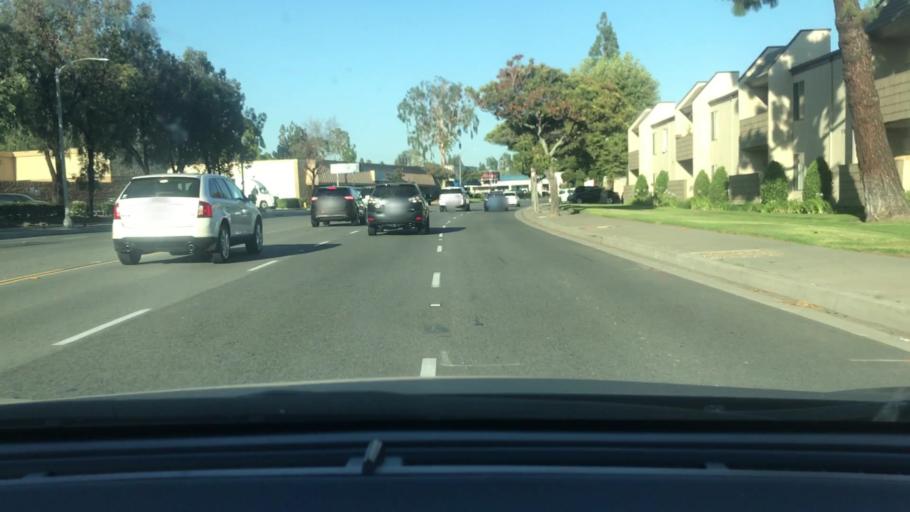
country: US
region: California
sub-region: Orange County
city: Placentia
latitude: 33.8891
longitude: -117.8730
